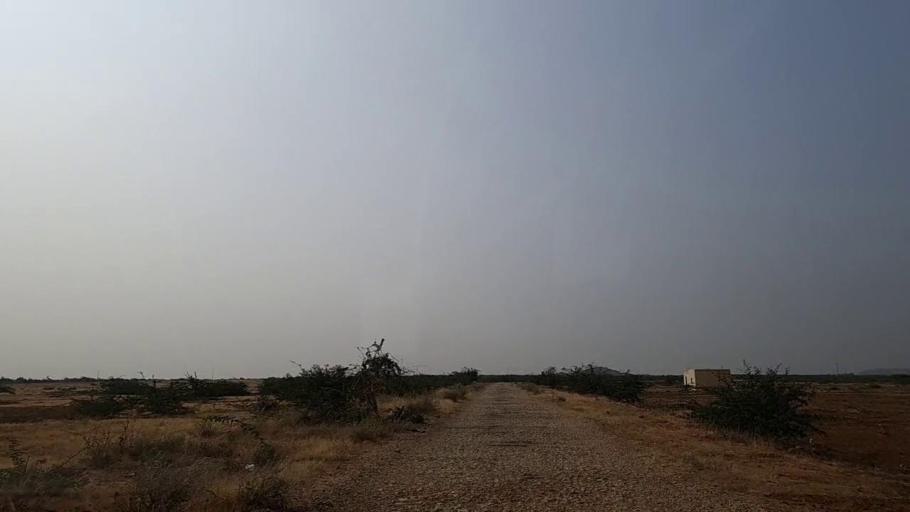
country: PK
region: Sindh
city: Thatta
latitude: 24.7234
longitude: 67.8325
